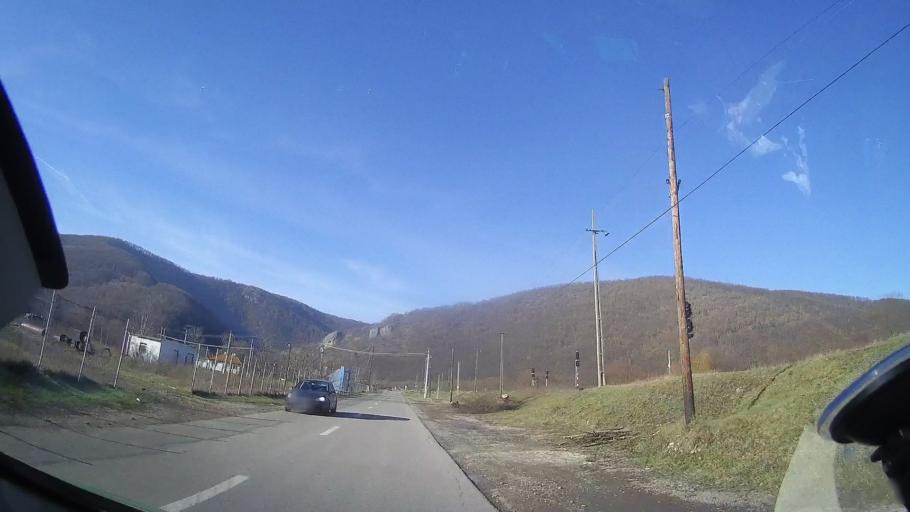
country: RO
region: Bihor
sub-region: Comuna Suncuius
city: Suncuius
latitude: 46.9500
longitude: 22.5333
